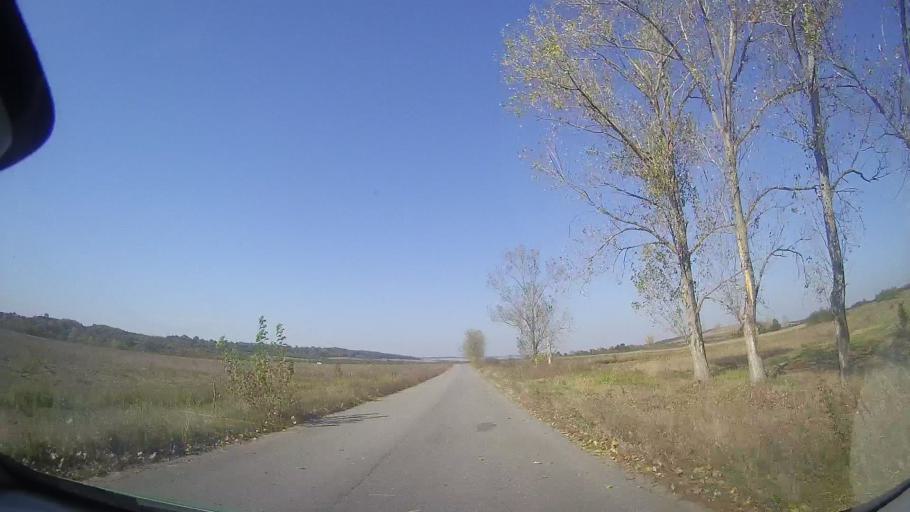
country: RO
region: Timis
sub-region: Comuna Ghizela
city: Ghizela
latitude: 45.8226
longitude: 21.7327
